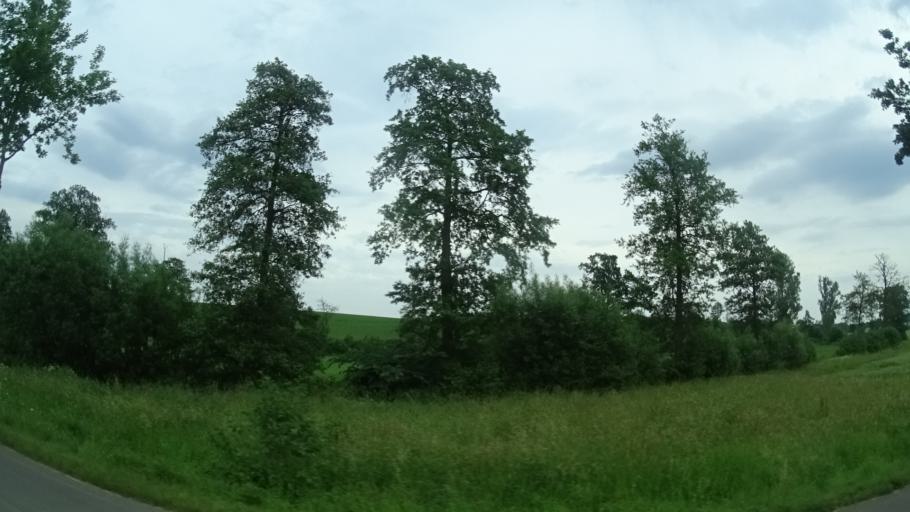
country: DE
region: North Rhine-Westphalia
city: Brakel
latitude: 51.7874
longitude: 9.1979
